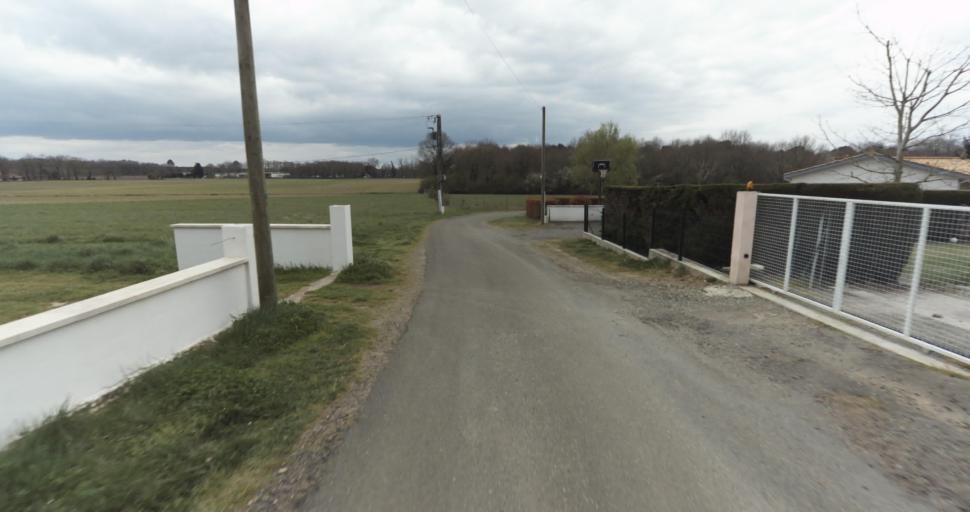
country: FR
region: Aquitaine
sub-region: Departement des Landes
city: Roquefort
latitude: 44.0215
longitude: -0.3367
